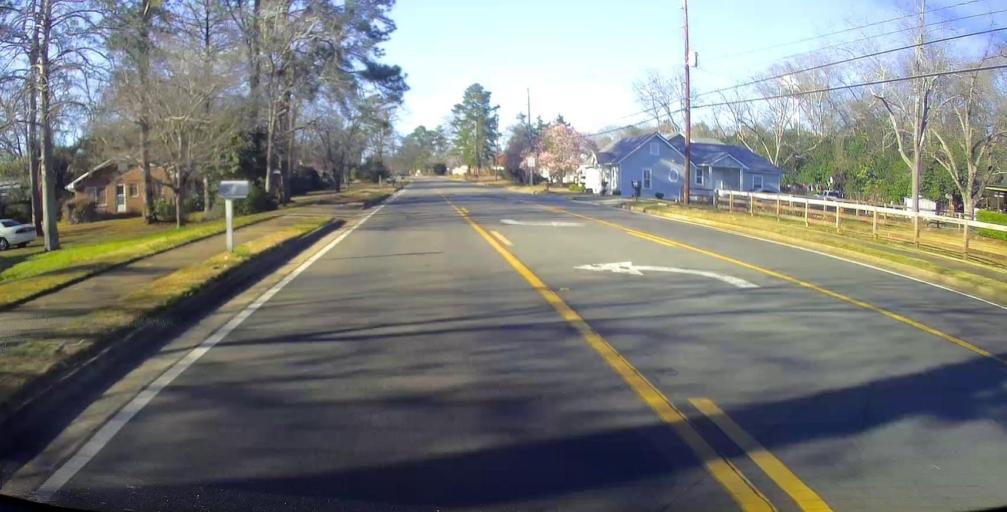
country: US
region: Georgia
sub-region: Sumter County
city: Americus
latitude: 32.0499
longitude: -84.2246
